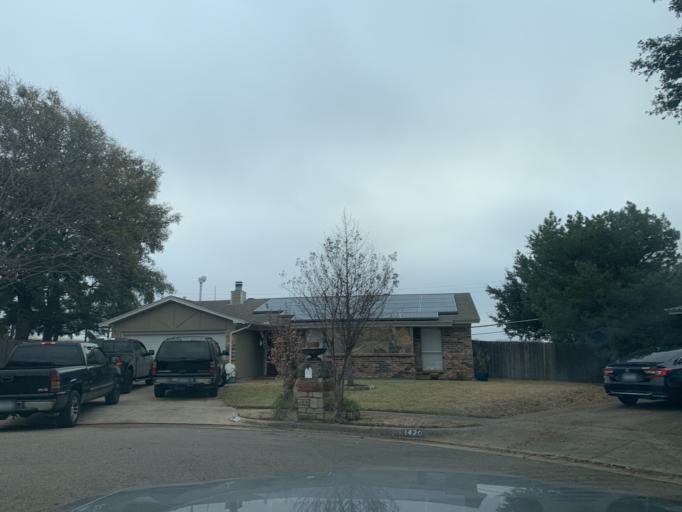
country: US
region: Texas
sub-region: Tarrant County
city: Bedford
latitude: 32.8352
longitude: -97.1451
